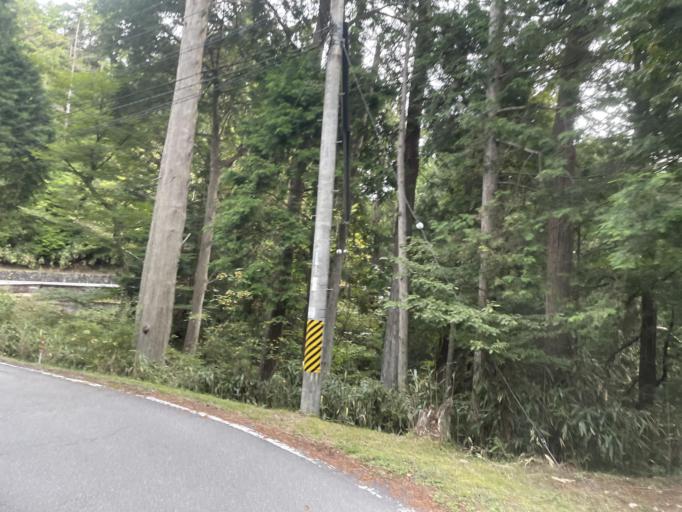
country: JP
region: Wakayama
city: Koya
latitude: 34.2241
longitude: 135.5758
